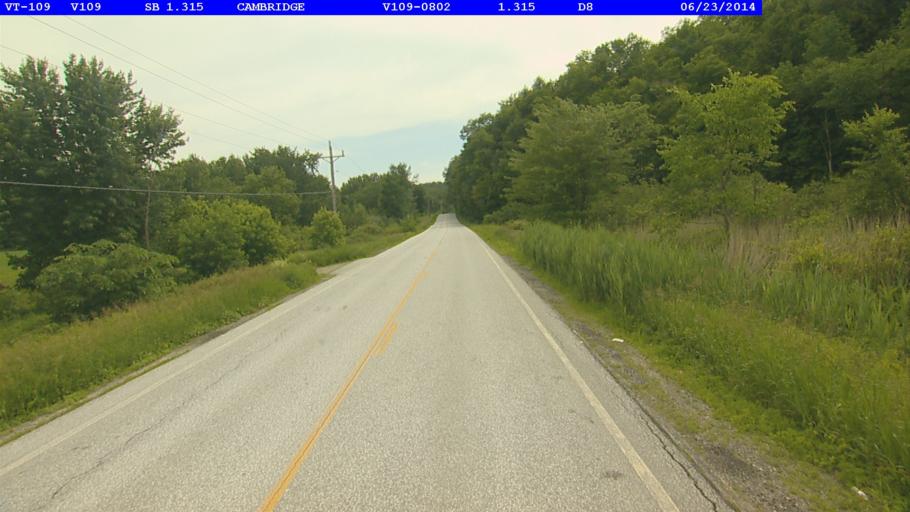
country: US
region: Vermont
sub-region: Lamoille County
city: Johnson
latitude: 44.6596
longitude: -72.8072
